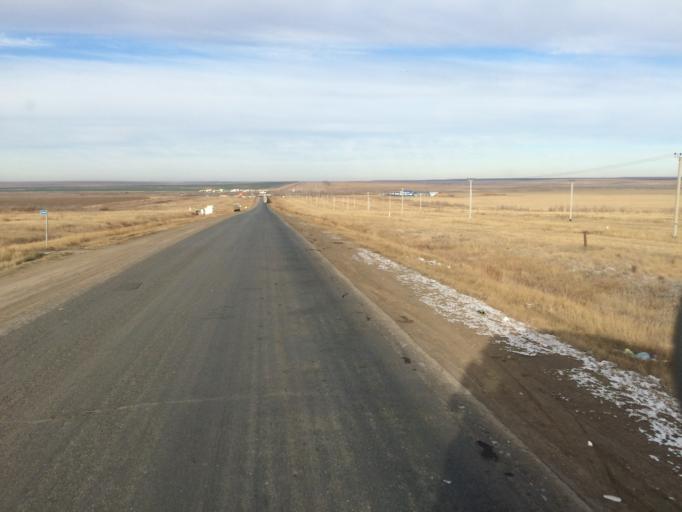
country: KZ
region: Batys Qazaqstan
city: Peremetnoe
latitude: 51.6554
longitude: 51.0097
